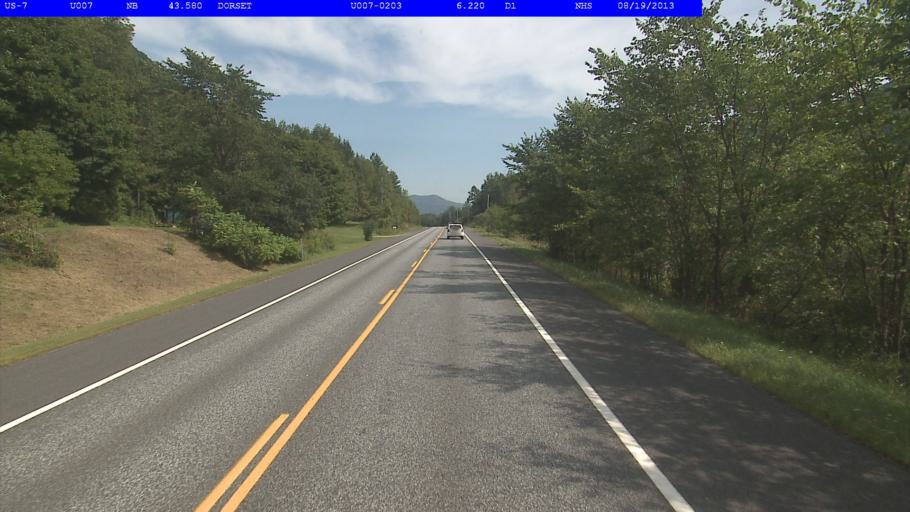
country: US
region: Vermont
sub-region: Bennington County
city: Manchester Center
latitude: 43.2979
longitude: -72.9969
